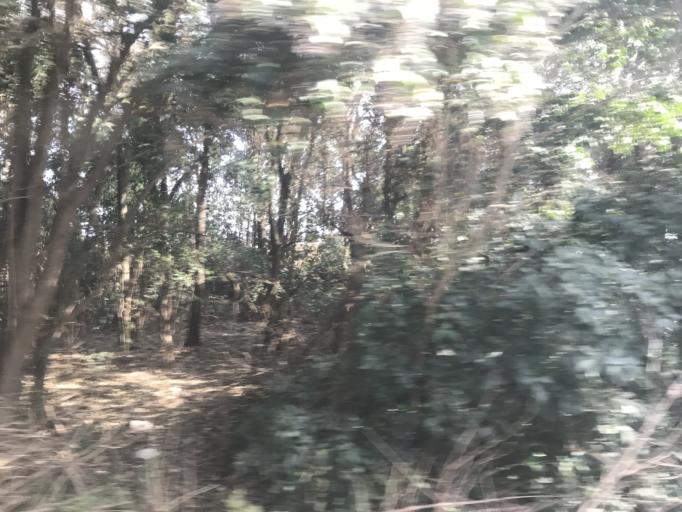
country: AR
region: Cordoba
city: Laguna Larga
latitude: -31.7920
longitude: -63.7900
